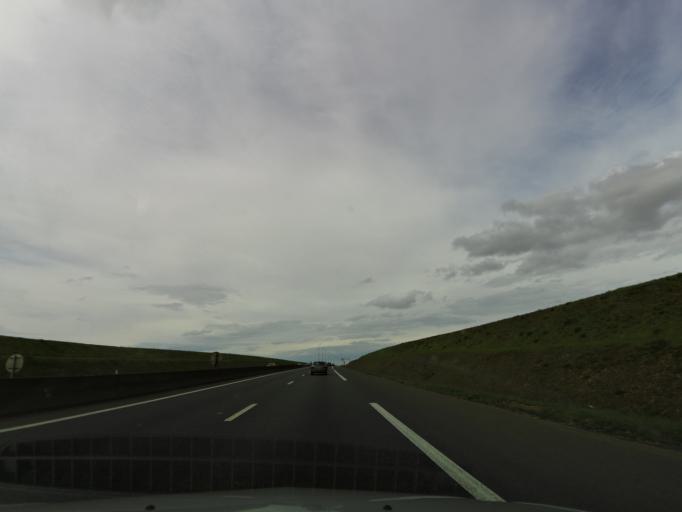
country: FR
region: Lower Normandy
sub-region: Departement du Calvados
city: Eterville
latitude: 49.1463
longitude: -0.4091
